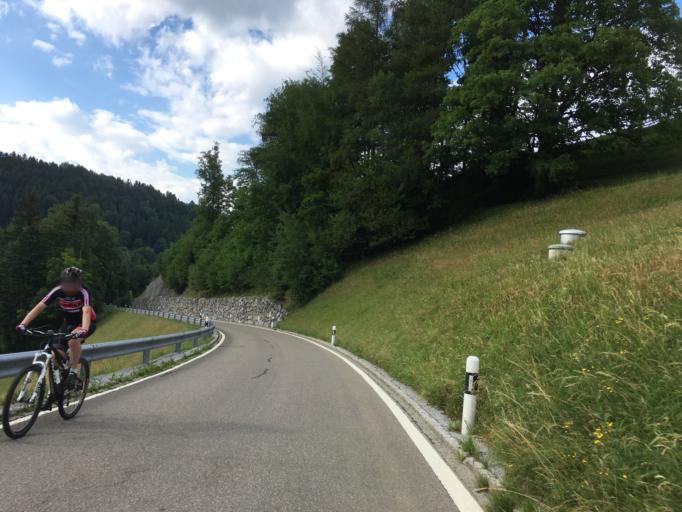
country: CH
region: Saint Gallen
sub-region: Wahlkreis Toggenburg
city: Lichtensteig
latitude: 47.3231
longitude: 9.0665
